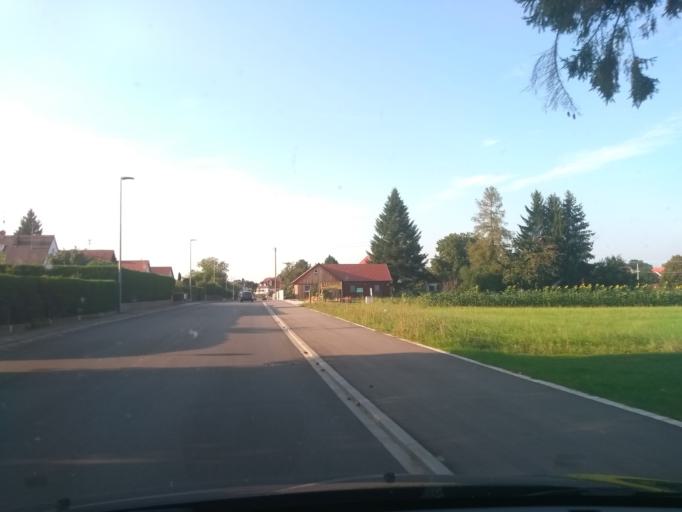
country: DE
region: Bavaria
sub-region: Upper Bavaria
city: Markt Indersdorf
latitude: 48.3499
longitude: 11.3833
